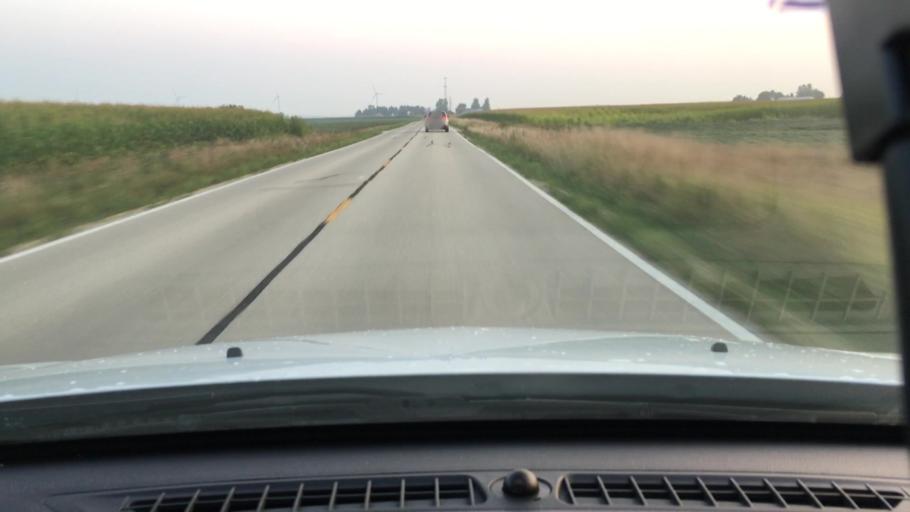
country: US
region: Illinois
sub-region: DeKalb County
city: Malta
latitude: 41.8553
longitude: -88.8478
